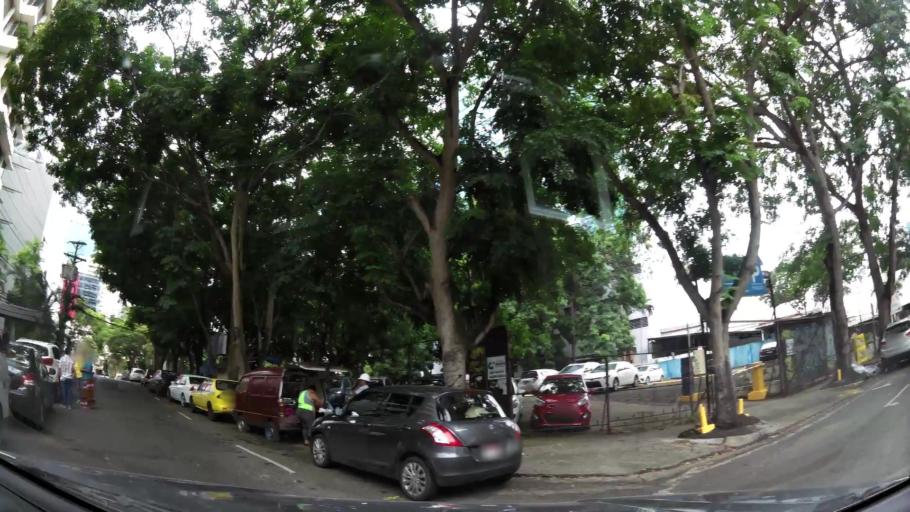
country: PA
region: Panama
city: Panama
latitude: 8.9815
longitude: -79.5231
